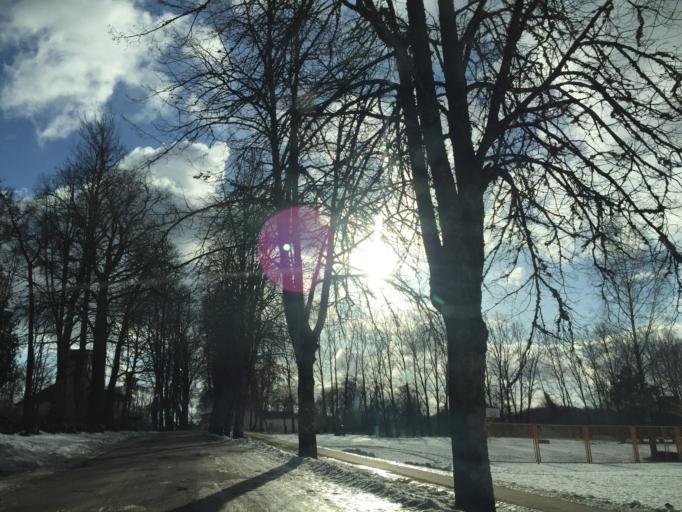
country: LV
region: Limbazu Rajons
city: Limbazi
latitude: 57.6107
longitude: 24.6086
